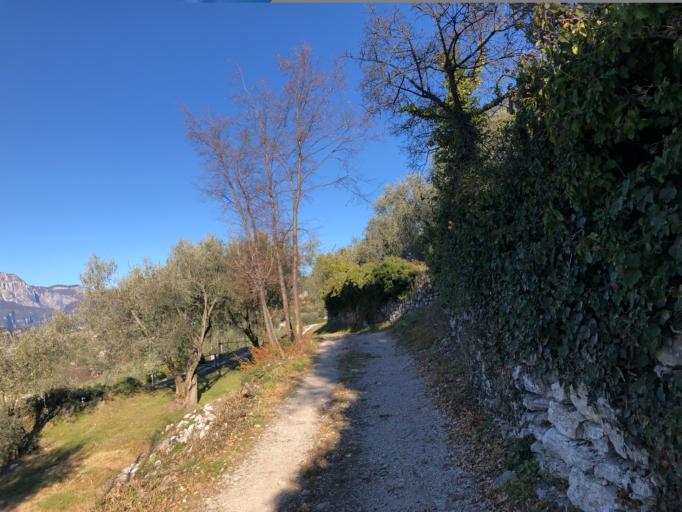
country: IT
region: Trentino-Alto Adige
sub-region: Provincia di Trento
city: Torbole sul Garda
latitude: 45.8670
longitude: 10.8851
